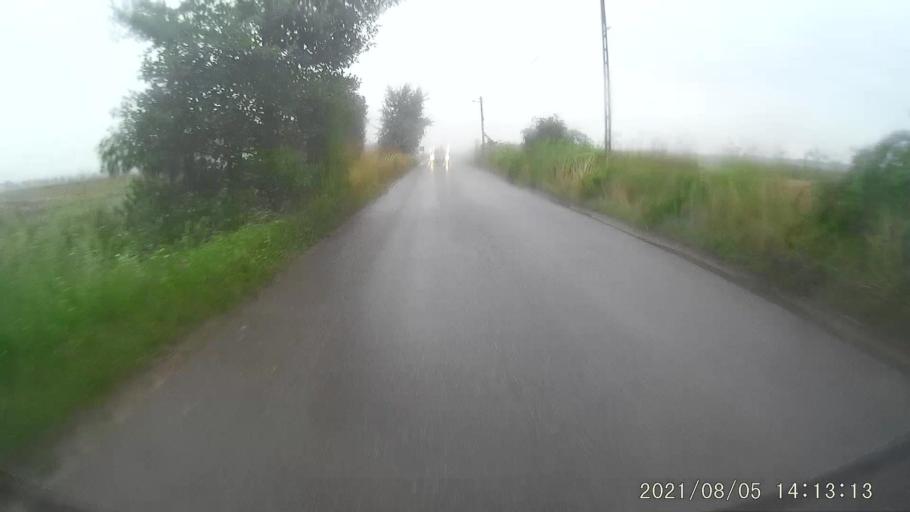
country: PL
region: Opole Voivodeship
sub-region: Powiat krapkowicki
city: Strzeleczki
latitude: 50.4699
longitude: 17.7497
